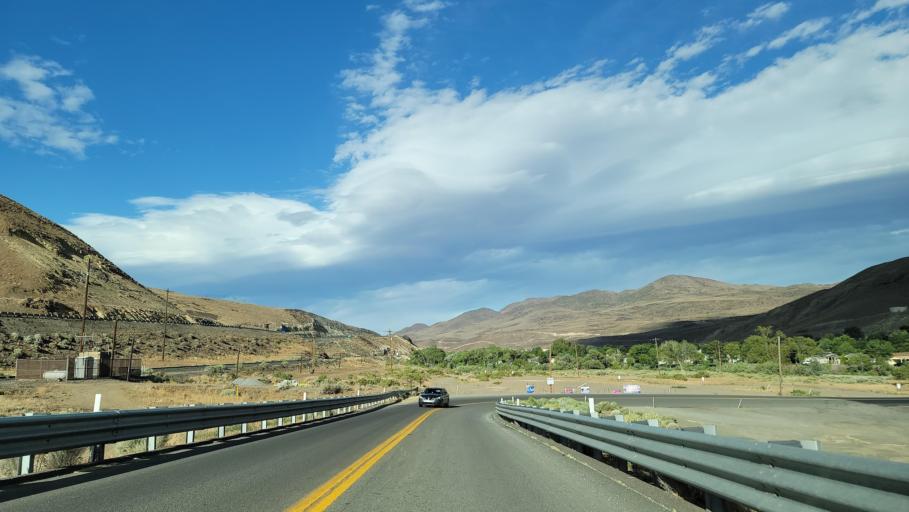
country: US
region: Nevada
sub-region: Washoe County
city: Sparks
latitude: 39.5108
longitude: -119.6507
